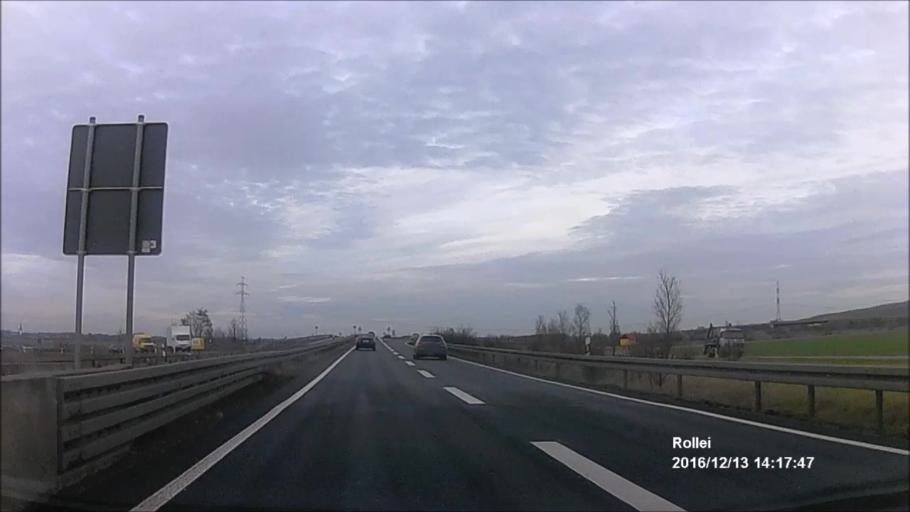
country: DE
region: Thuringia
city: Kleinmolsen
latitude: 51.0354
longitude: 11.0643
